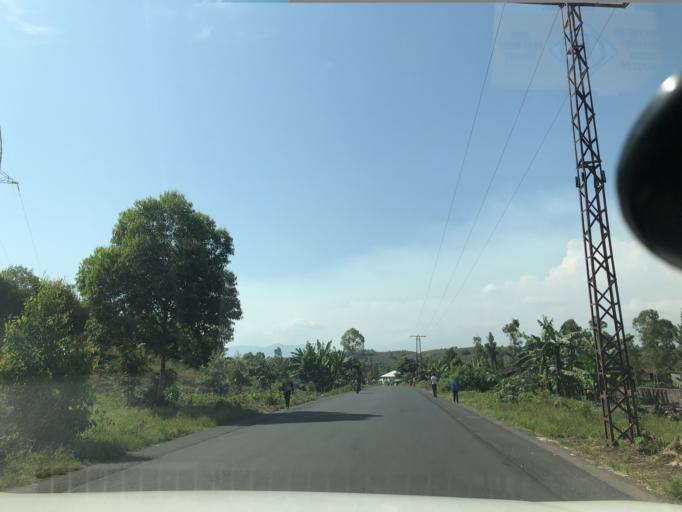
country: CD
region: Nord Kivu
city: Sake
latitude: -1.6110
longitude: 29.1401
